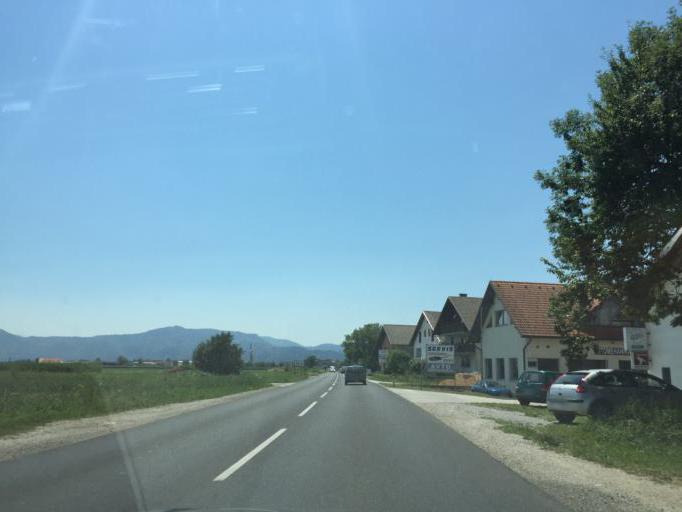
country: SI
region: Kranj
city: Zgornje Bitnje
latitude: 46.2056
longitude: 14.3339
